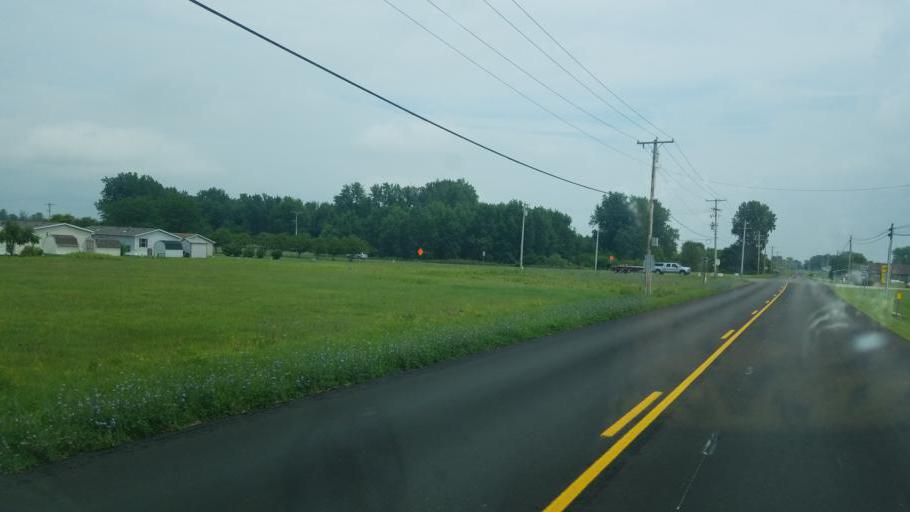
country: US
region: Ohio
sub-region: Logan County
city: Russells Point
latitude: 40.4699
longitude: -83.8576
